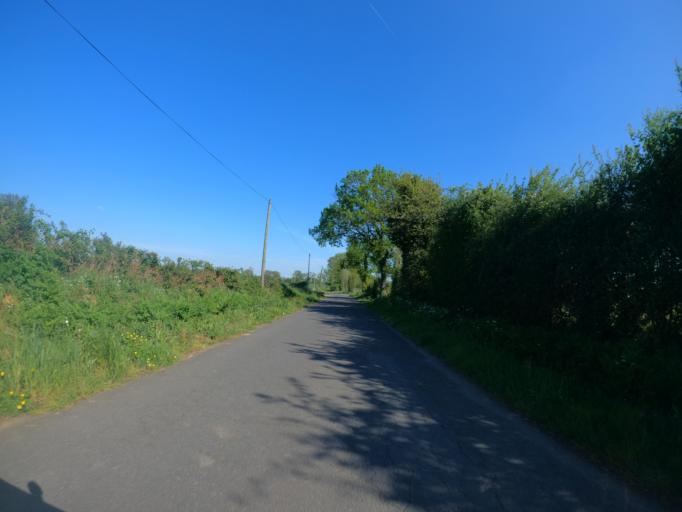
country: FR
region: Poitou-Charentes
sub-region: Departement des Deux-Sevres
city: Moncoutant
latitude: 46.6824
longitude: -0.5268
